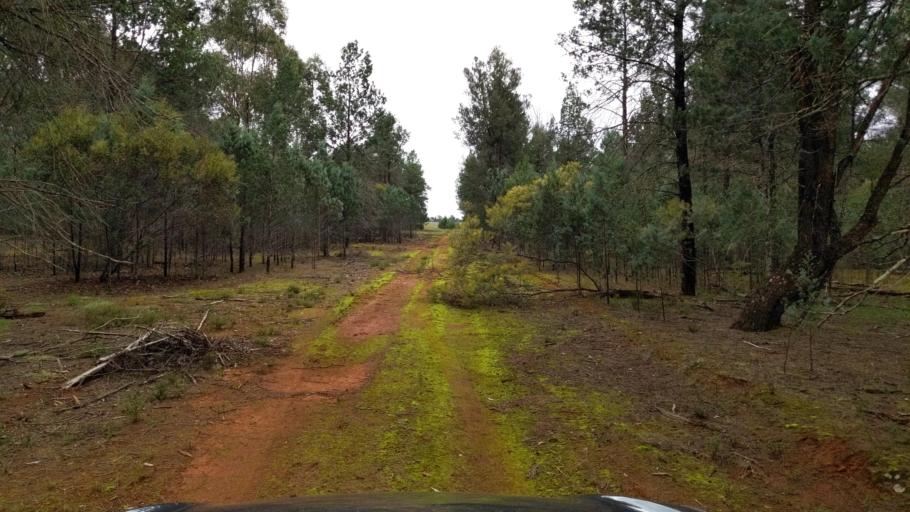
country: AU
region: New South Wales
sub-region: Coolamon
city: Coolamon
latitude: -34.8278
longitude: 146.9360
